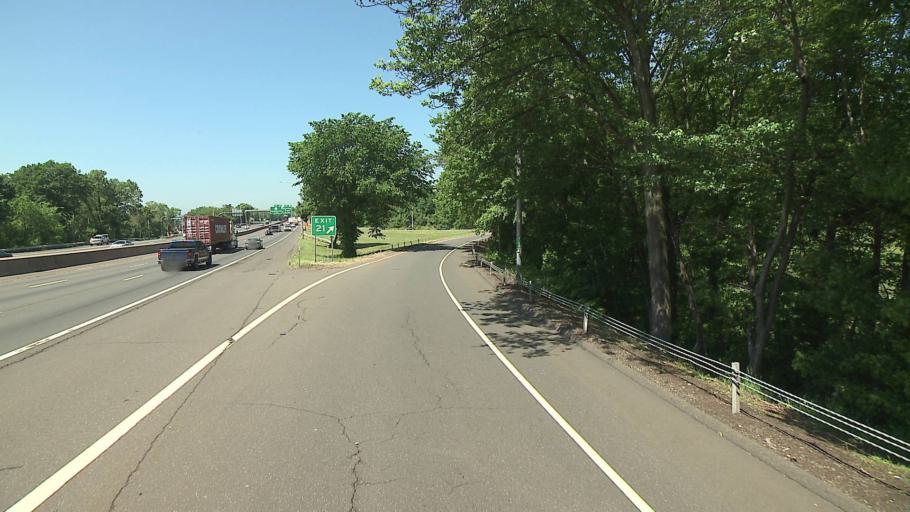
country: US
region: Connecticut
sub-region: Fairfield County
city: Fairfield
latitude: 41.1454
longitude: -73.2623
